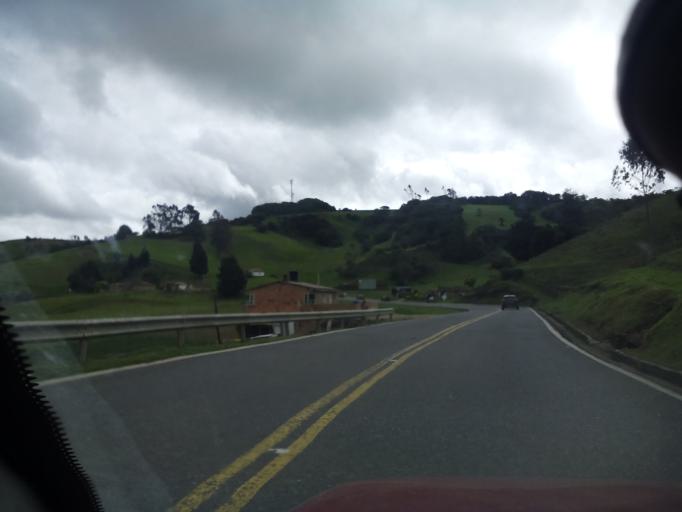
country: CO
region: Boyaca
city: Combita
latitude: 5.6601
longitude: -73.3595
